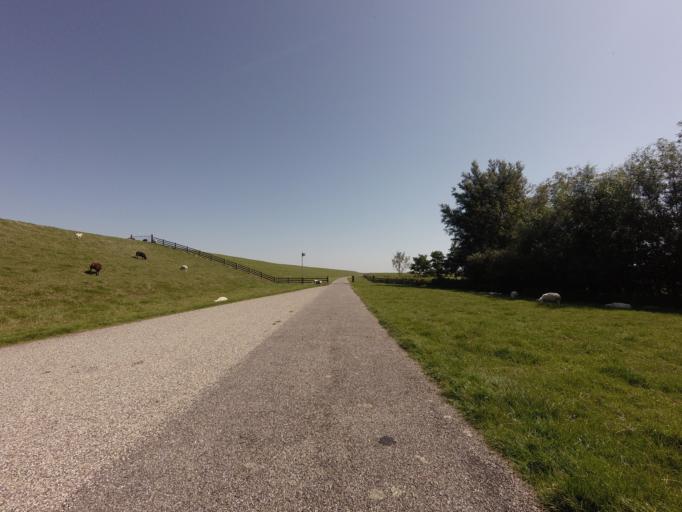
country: NL
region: Friesland
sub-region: Gemeente Dongeradeel
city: Anjum
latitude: 53.4017
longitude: 6.0906
